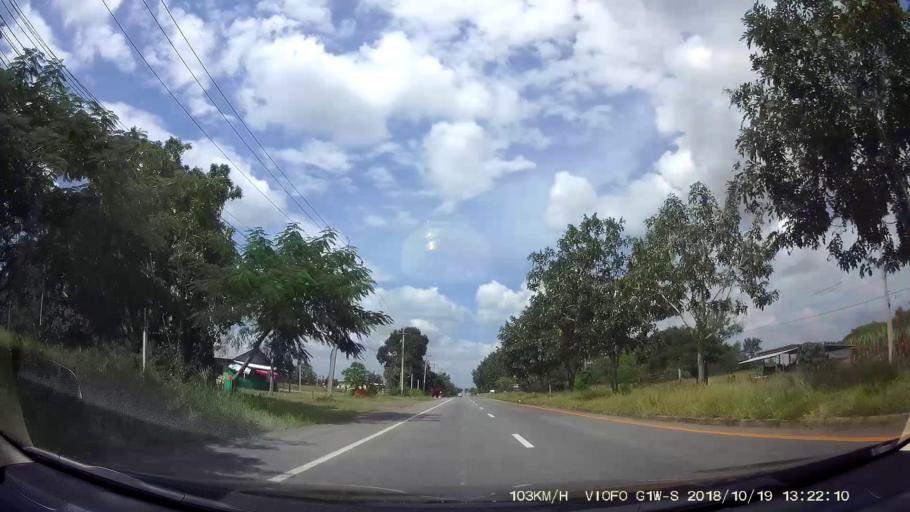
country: TH
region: Chaiyaphum
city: Chatturat
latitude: 15.4732
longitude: 101.8243
